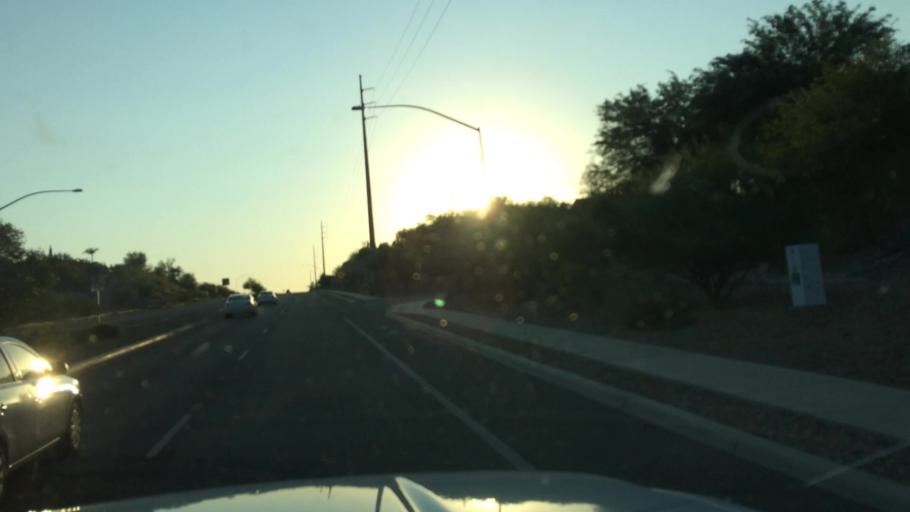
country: US
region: Arizona
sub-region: Pima County
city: Catalina Foothills
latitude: 32.3089
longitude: -110.8479
